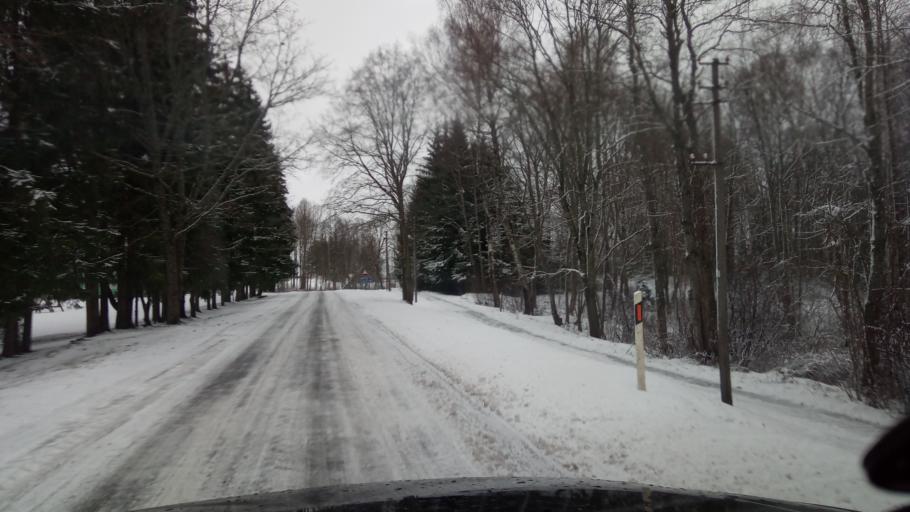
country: LT
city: Zarasai
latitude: 55.6292
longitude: 25.9552
